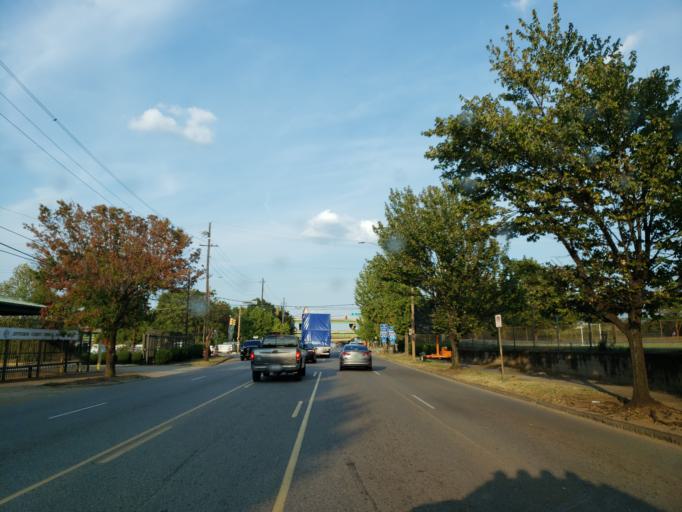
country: US
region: Alabama
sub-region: Jefferson County
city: Birmingham
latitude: 33.5245
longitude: -86.8044
